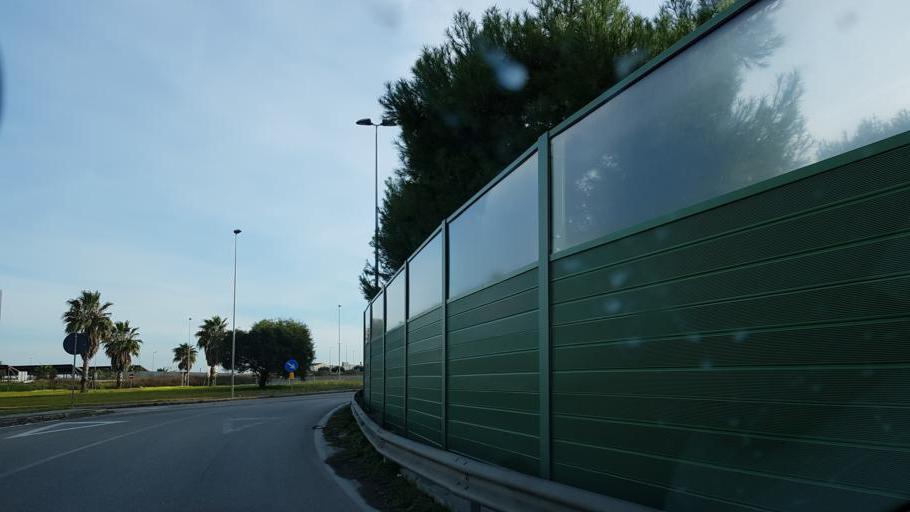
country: IT
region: Apulia
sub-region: Provincia di Brindisi
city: La Rosa
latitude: 40.6288
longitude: 17.9608
